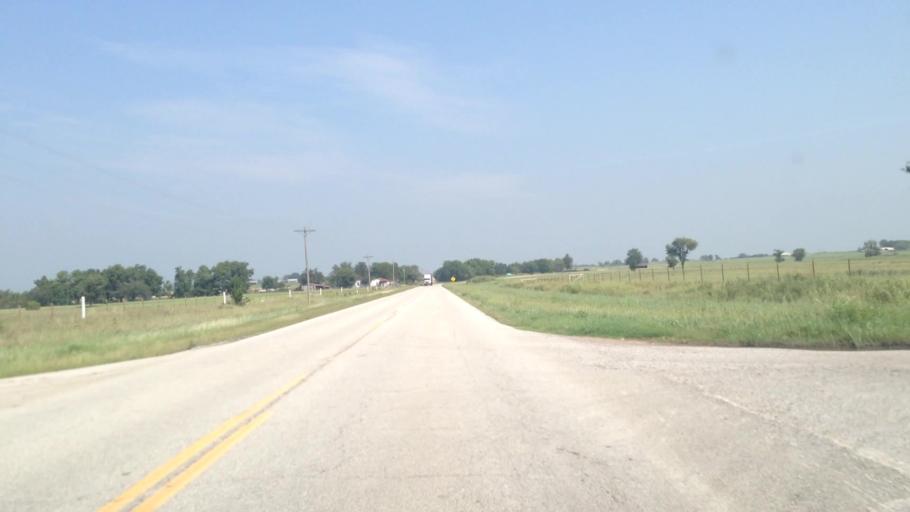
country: US
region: Oklahoma
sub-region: Craig County
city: Vinita
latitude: 36.8154
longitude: -95.1436
